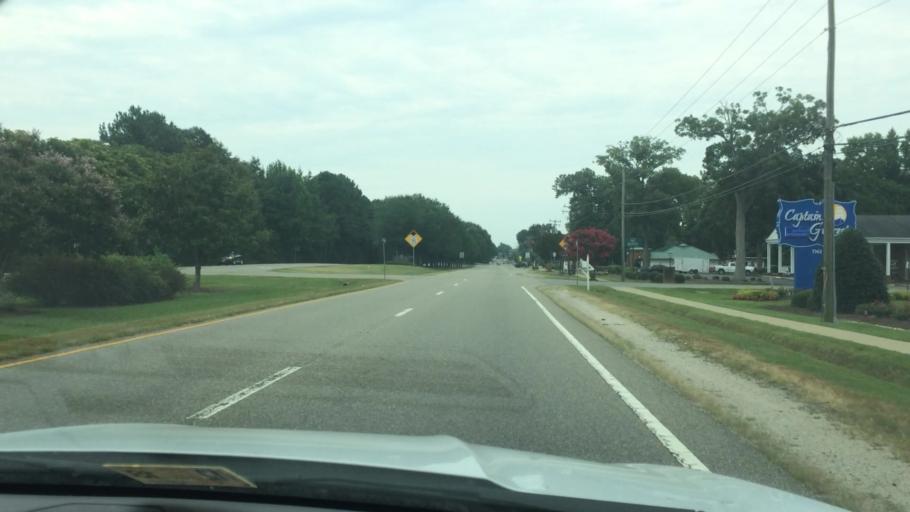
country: US
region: Virginia
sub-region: James City County
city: Williamsburg
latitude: 37.3112
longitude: -76.7318
